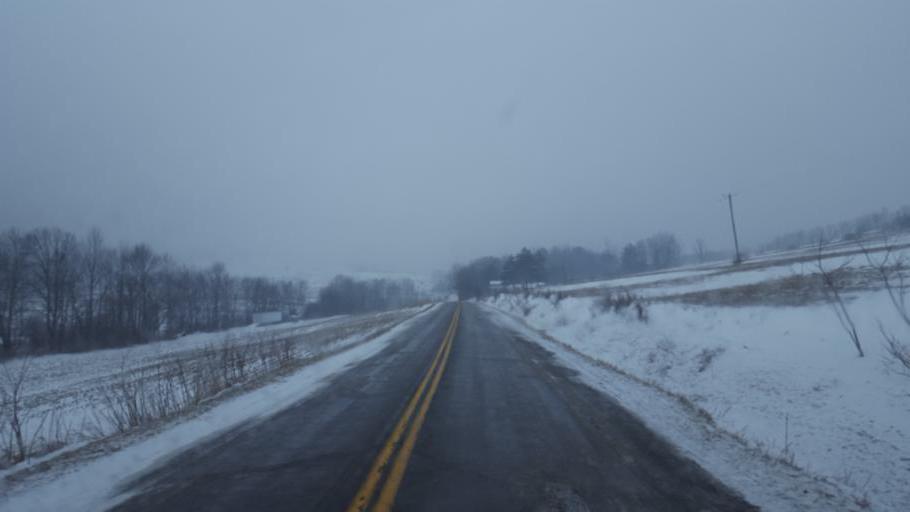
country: US
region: New York
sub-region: Steuben County
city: Canisteo
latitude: 42.1372
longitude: -77.5439
